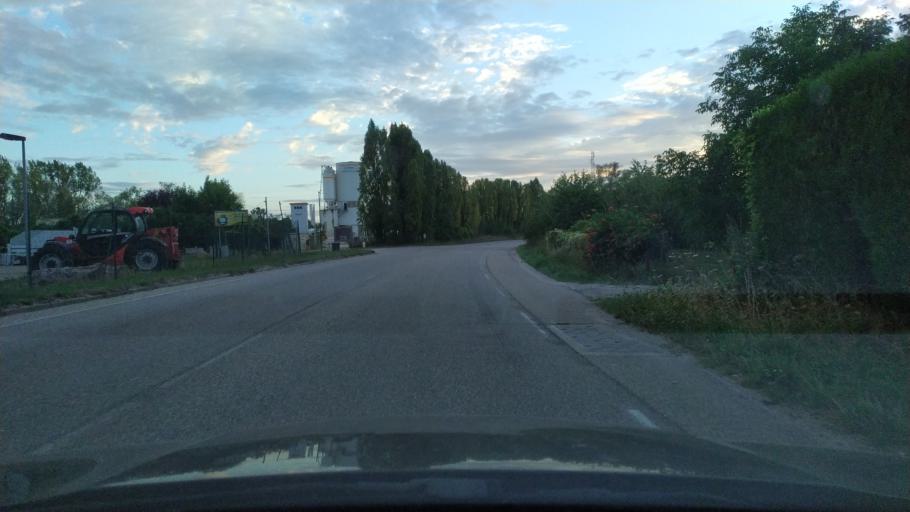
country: FR
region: Lorraine
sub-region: Departement de la Moselle
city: Moulins-les-Metz
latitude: 49.0993
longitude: 6.1061
